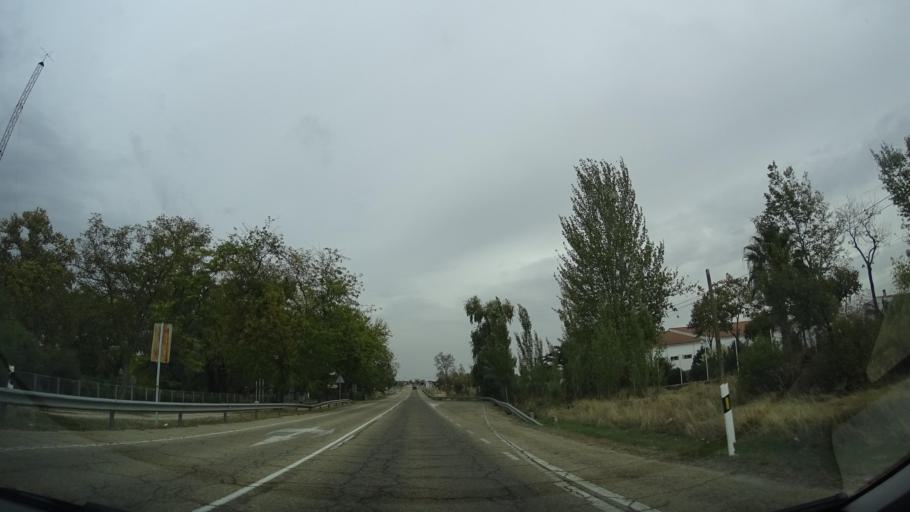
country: ES
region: Extremadura
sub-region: Provincia de Caceres
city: Trujillo
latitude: 39.4796
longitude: -5.8552
